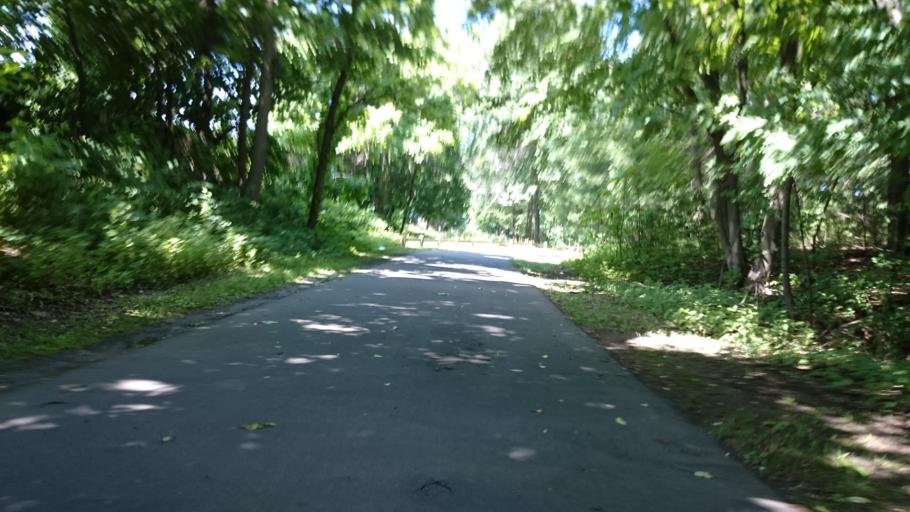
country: US
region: Connecticut
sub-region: New Haven County
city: New Haven
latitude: 41.3478
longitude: -72.9304
